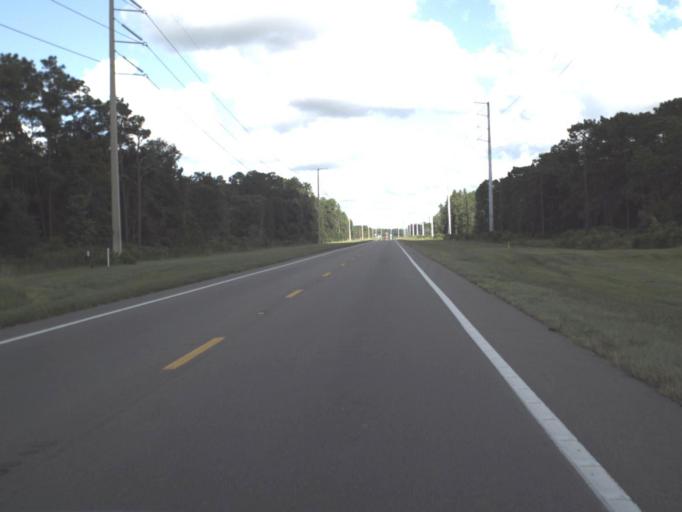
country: US
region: Florida
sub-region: Polk County
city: Kathleen
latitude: 28.2307
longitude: -82.0354
